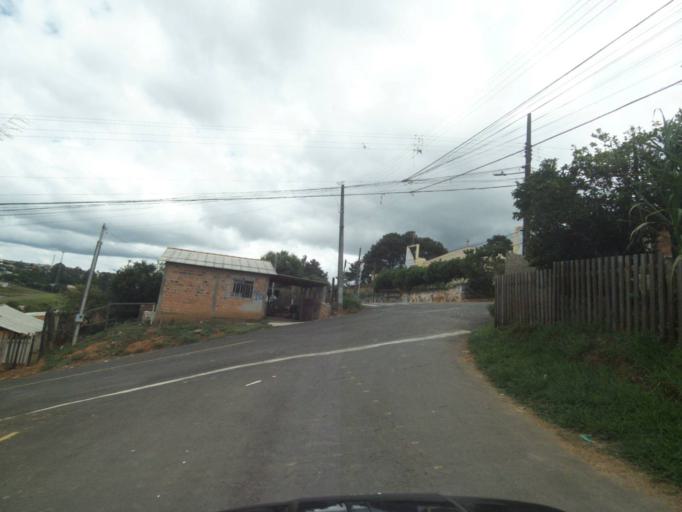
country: BR
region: Parana
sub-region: Telemaco Borba
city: Telemaco Borba
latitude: -24.3123
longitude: -50.6444
